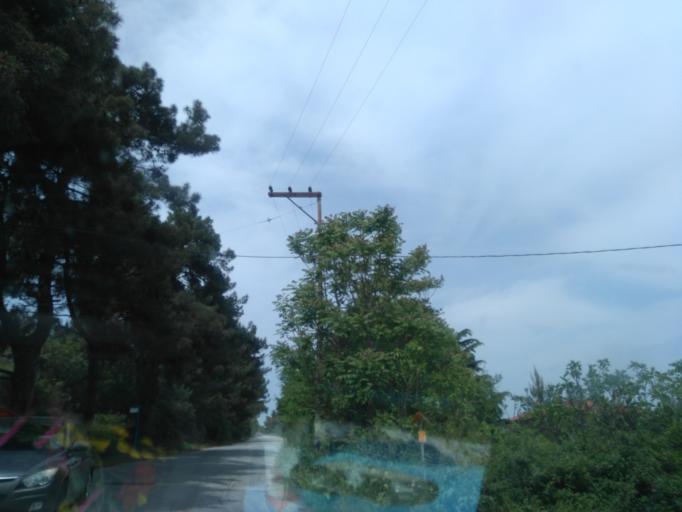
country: GR
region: Central Macedonia
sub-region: Nomos Thessalonikis
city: Lagyna
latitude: 40.7248
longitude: 22.9930
